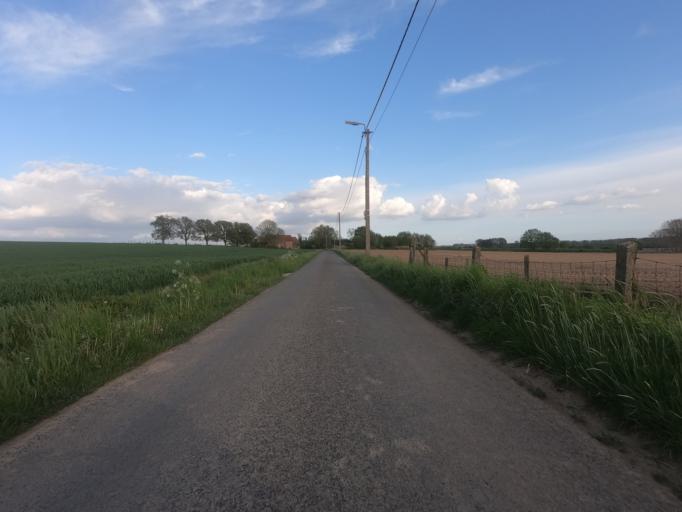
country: BE
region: Flanders
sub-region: Provincie Vlaams-Brabant
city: Herne
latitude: 50.7563
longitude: 4.0128
